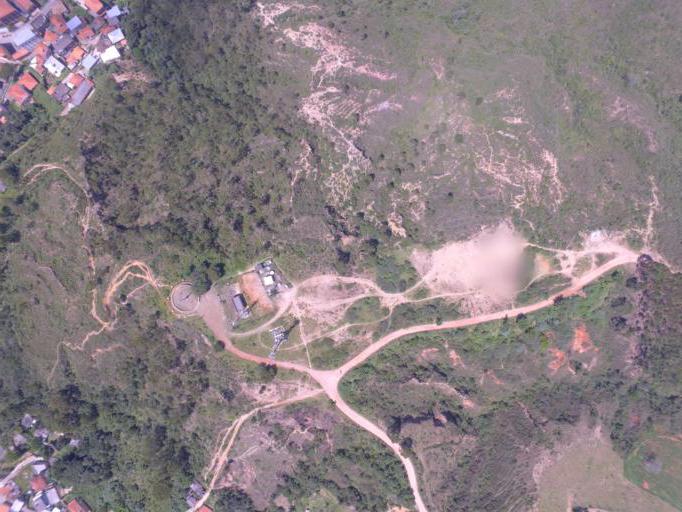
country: BR
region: Minas Gerais
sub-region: Tiradentes
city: Tiradentes
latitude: -21.0538
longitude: -44.0795
